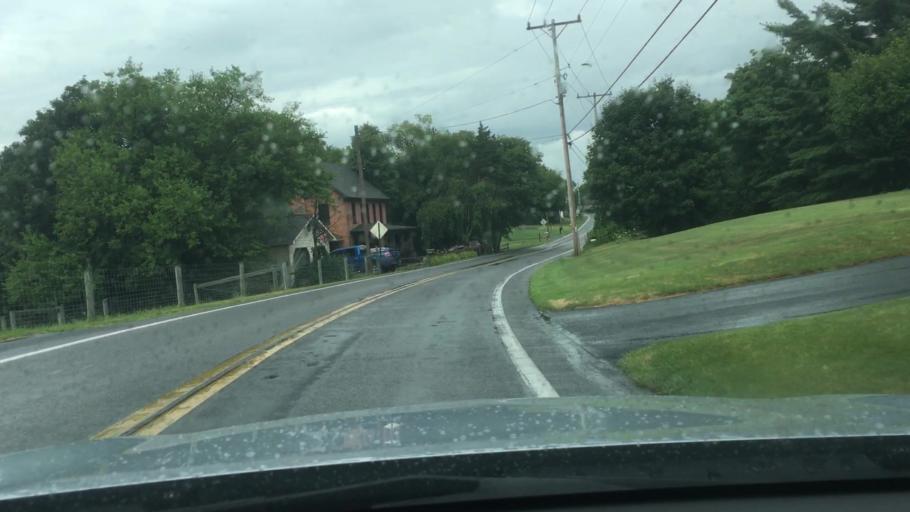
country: US
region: Pennsylvania
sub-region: Franklin County
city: Greencastle
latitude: 39.8691
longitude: -77.7346
